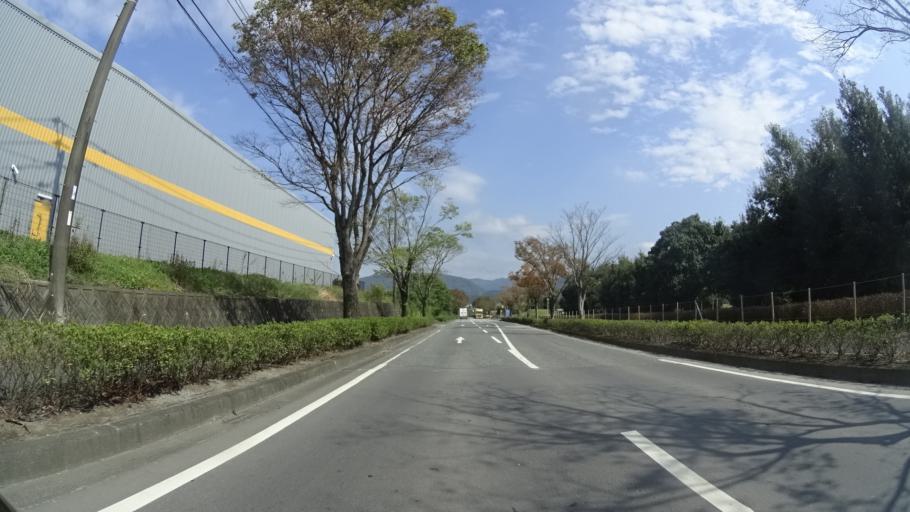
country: JP
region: Kumamoto
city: Kumamoto
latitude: 32.7488
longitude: 130.7945
